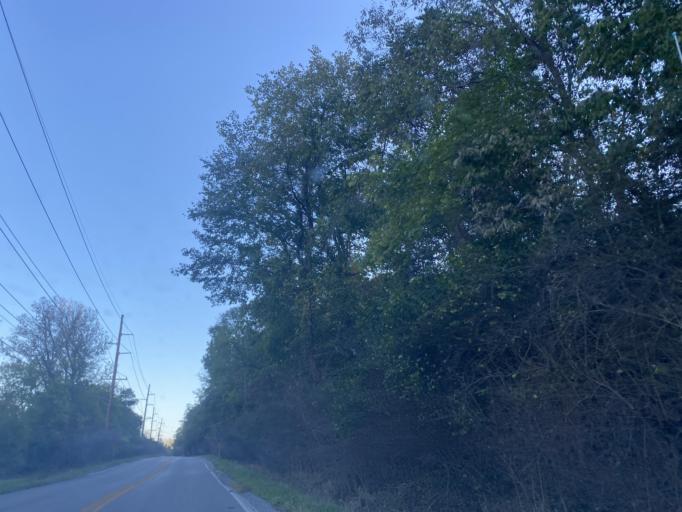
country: US
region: Kentucky
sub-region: Campbell County
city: Fort Thomas
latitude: 39.1046
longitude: -84.4431
